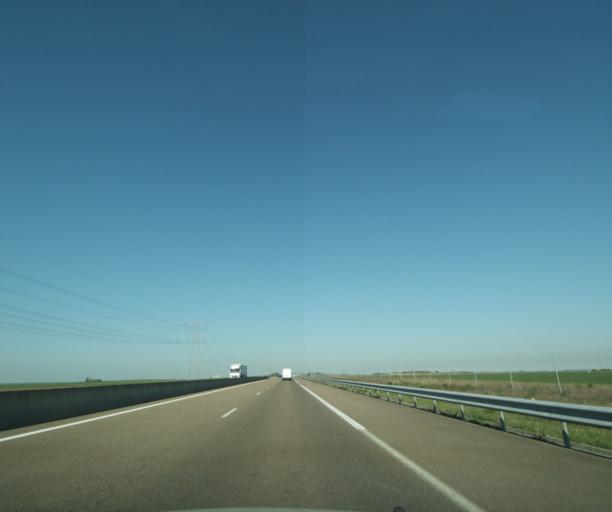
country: FR
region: Centre
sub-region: Departement du Loiret
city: Boynes
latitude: 48.0978
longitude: 2.3651
